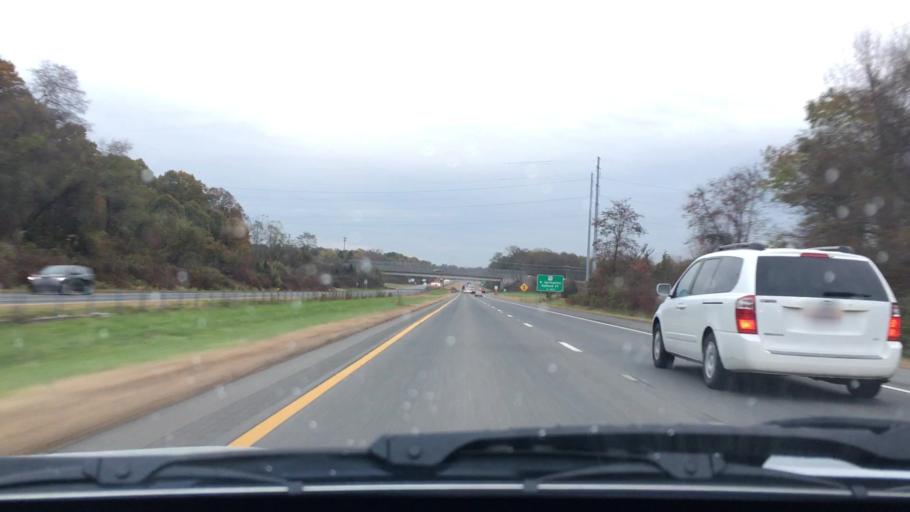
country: US
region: Massachusetts
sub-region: Hampden County
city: Agawam
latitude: 42.0695
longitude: -72.6447
